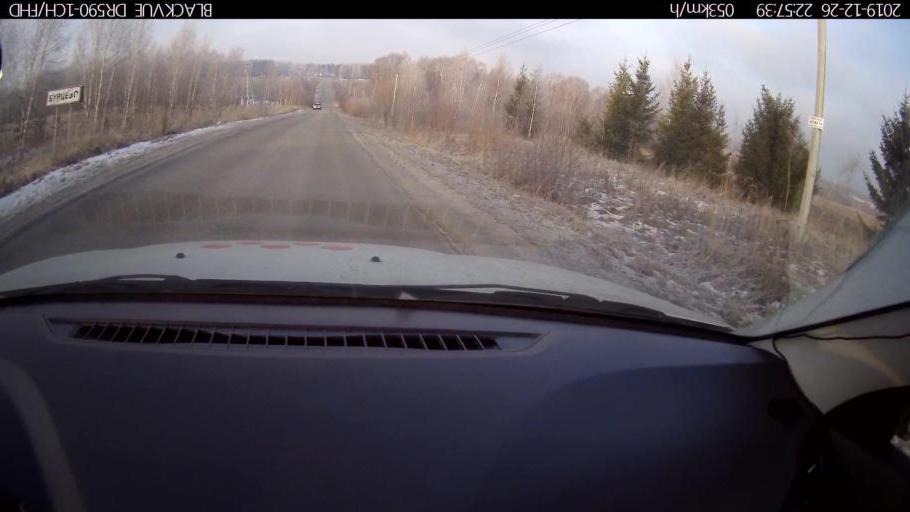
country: RU
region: Nizjnij Novgorod
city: Burevestnik
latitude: 56.1522
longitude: 43.7143
